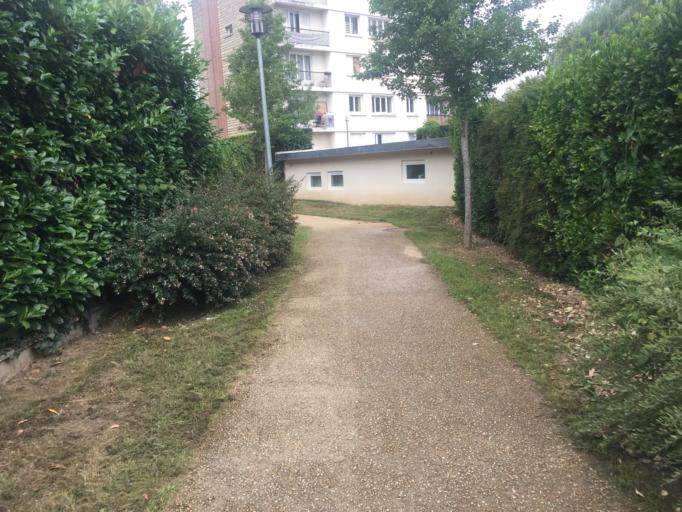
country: FR
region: Ile-de-France
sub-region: Departement des Yvelines
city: Bois-d'Arcy
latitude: 48.7995
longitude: 2.0330
